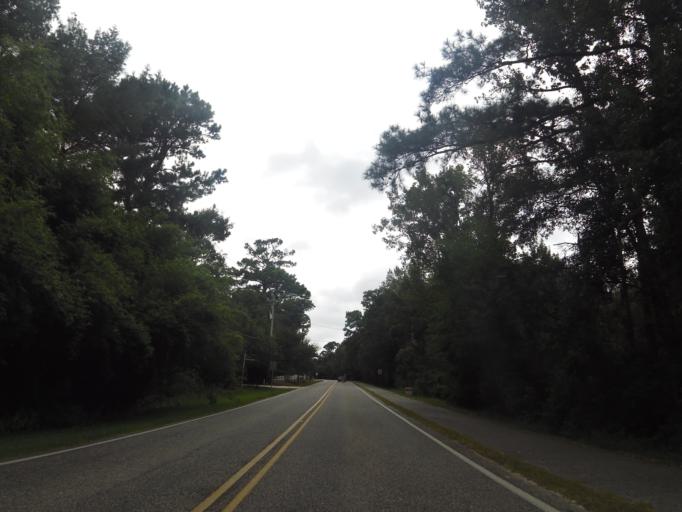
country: US
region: Alabama
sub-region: Baldwin County
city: Point Clear
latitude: 30.4817
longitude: -87.9279
